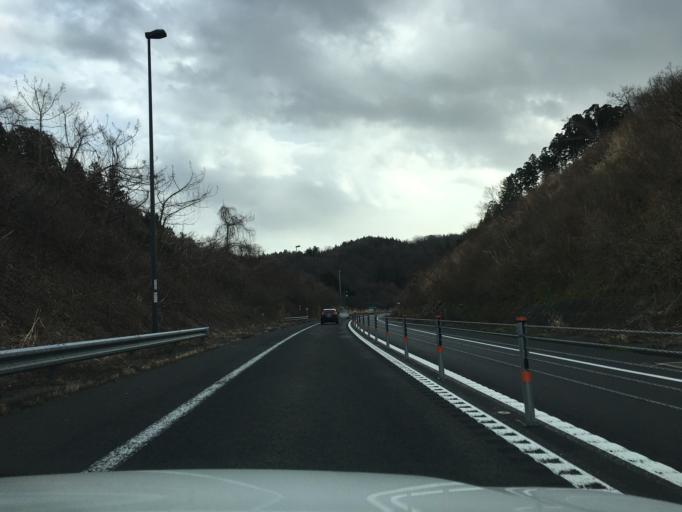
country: JP
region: Yamagata
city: Yuza
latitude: 39.3195
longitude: 140.0010
